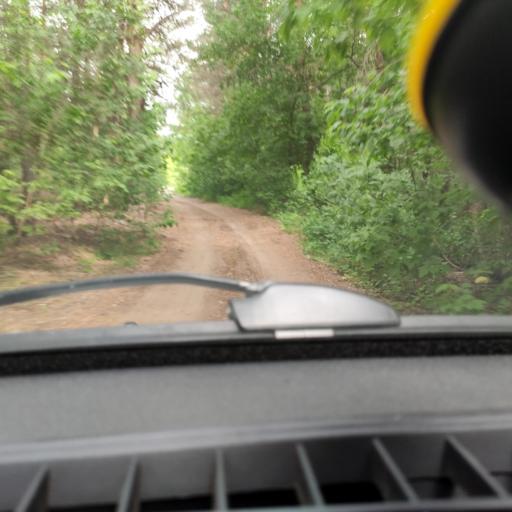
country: RU
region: Samara
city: Zhigulevsk
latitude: 53.5031
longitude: 49.5058
